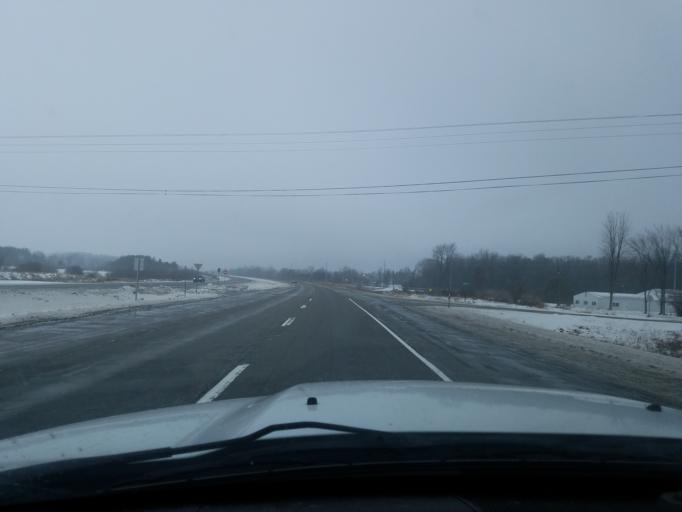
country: US
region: Indiana
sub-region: Fulton County
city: Rochester
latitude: 41.0103
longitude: -86.1682
